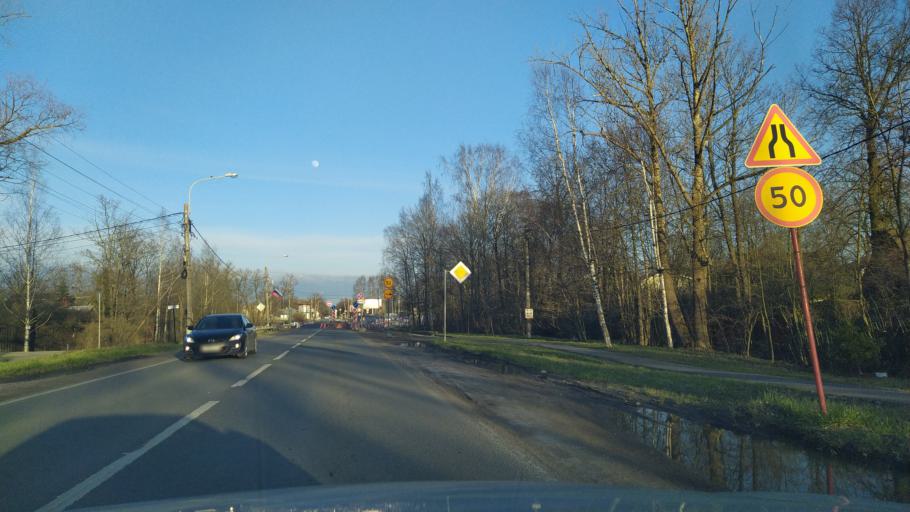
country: RU
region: St.-Petersburg
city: Aleksandrovskaya
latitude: 59.7345
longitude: 30.3378
